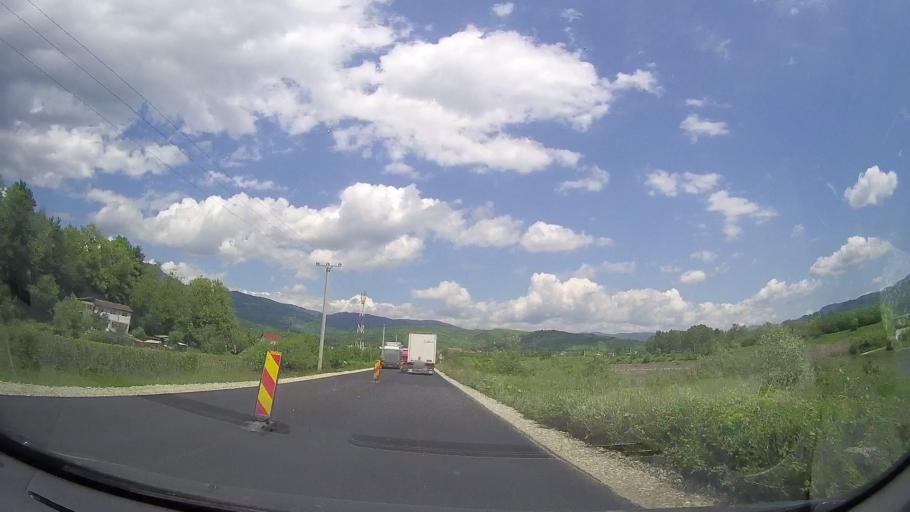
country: RO
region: Valcea
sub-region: Oras Calimanesti
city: Calimanesti
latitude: 45.2335
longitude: 24.3428
